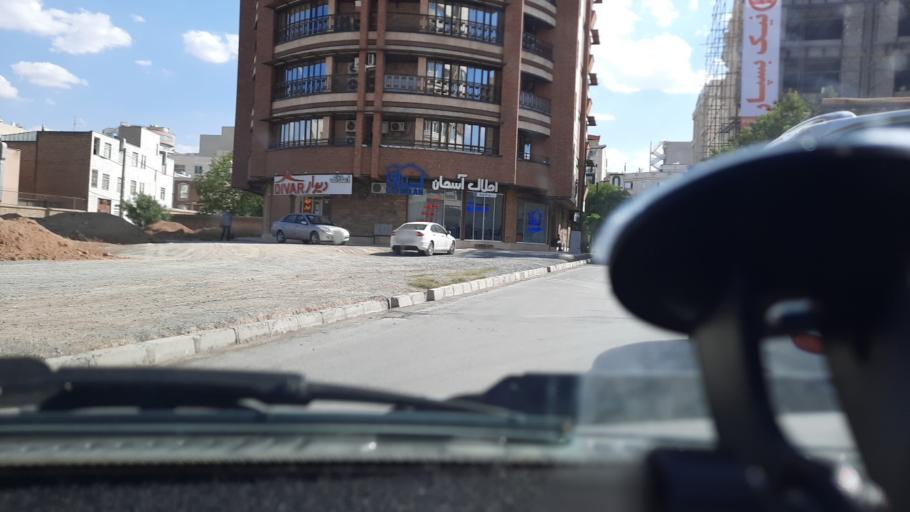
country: IR
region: Markazi
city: Arak
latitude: 34.0812
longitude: 49.6891
